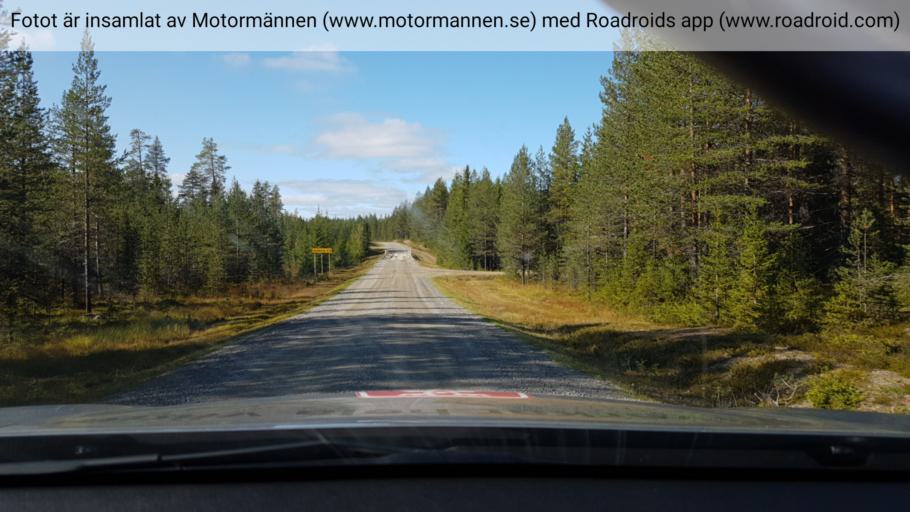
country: SE
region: Vaesterbotten
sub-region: Mala Kommun
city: Mala
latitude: 65.2127
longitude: 19.1071
